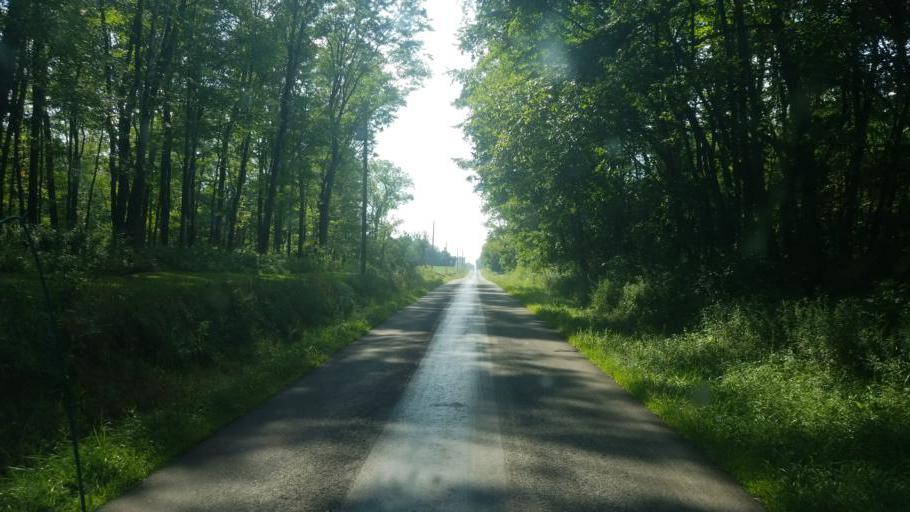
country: US
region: Ohio
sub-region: Wayne County
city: West Salem
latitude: 40.9524
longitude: -82.0424
